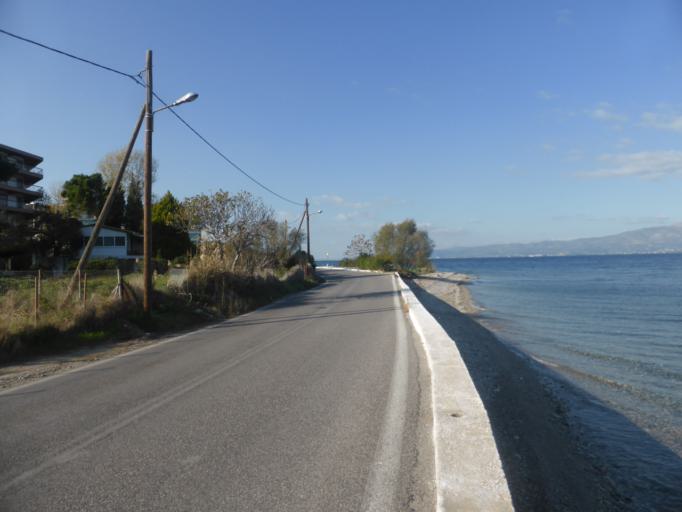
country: GR
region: Attica
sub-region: Nomarchia Anatolikis Attikis
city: Markopoulo Oropou
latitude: 38.3144
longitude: 23.8290
